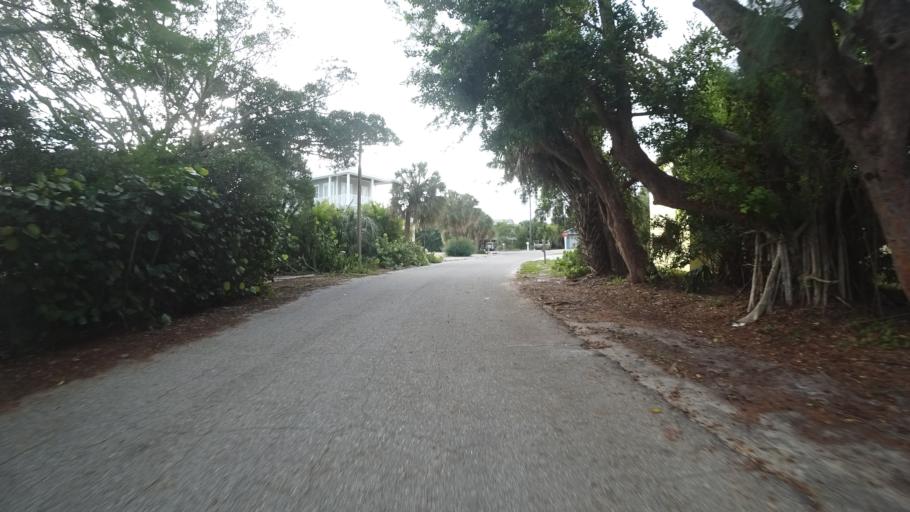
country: US
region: Florida
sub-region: Manatee County
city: Holmes Beach
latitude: 27.5044
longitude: -82.7159
